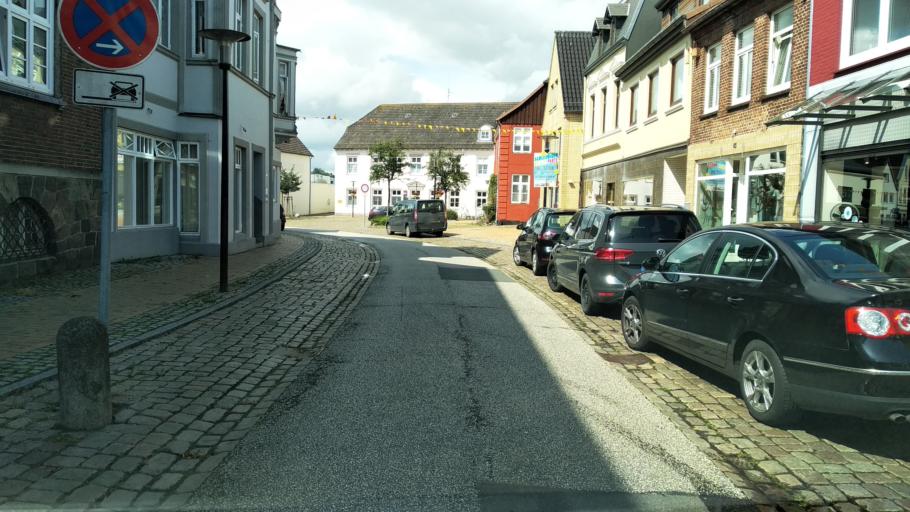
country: DE
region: Schleswig-Holstein
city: Busdorf
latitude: 54.5021
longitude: 9.5443
